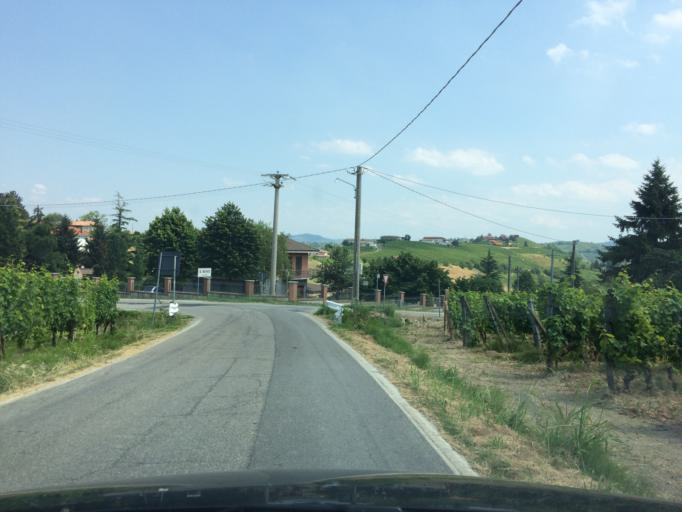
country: IT
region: Piedmont
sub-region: Provincia di Asti
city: Calosso
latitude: 44.7430
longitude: 8.2305
